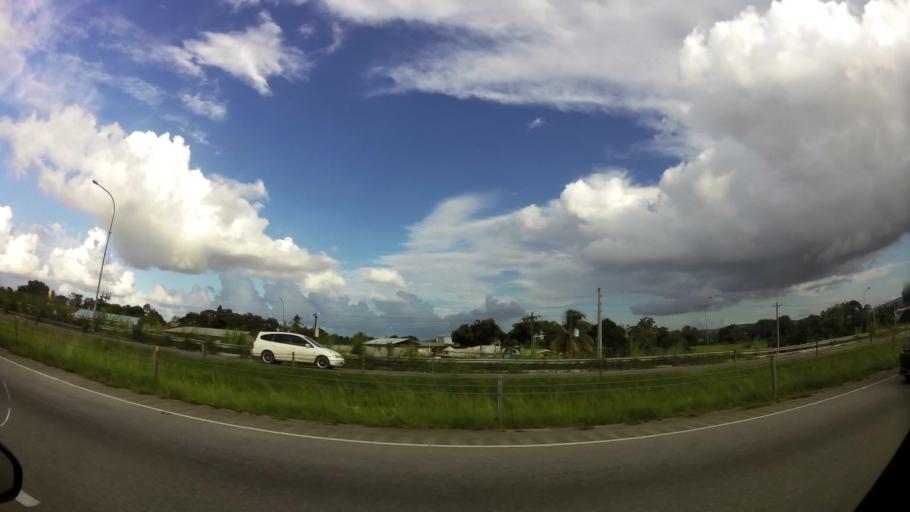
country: TT
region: Chaguanas
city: Chaguanas
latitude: 10.4607
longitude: -61.4106
